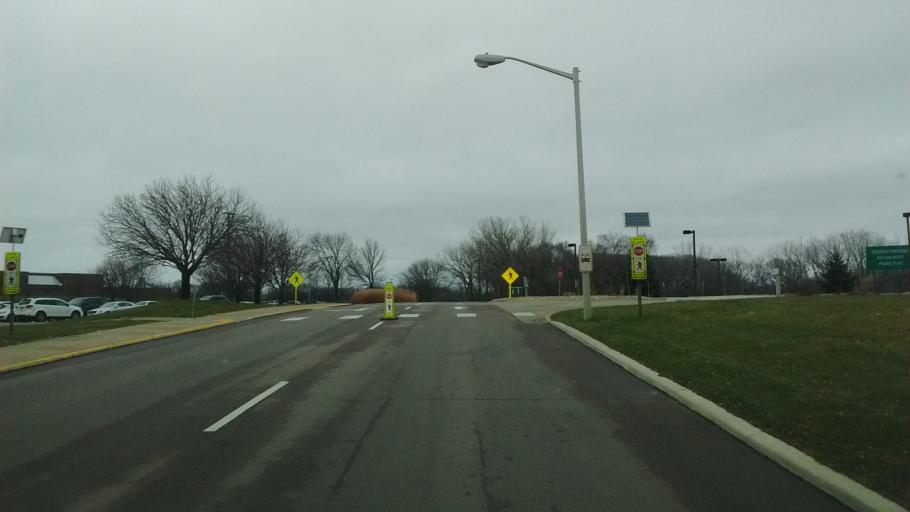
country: US
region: Iowa
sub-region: Woodbury County
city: Sioux City
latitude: 42.4820
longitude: -96.3470
